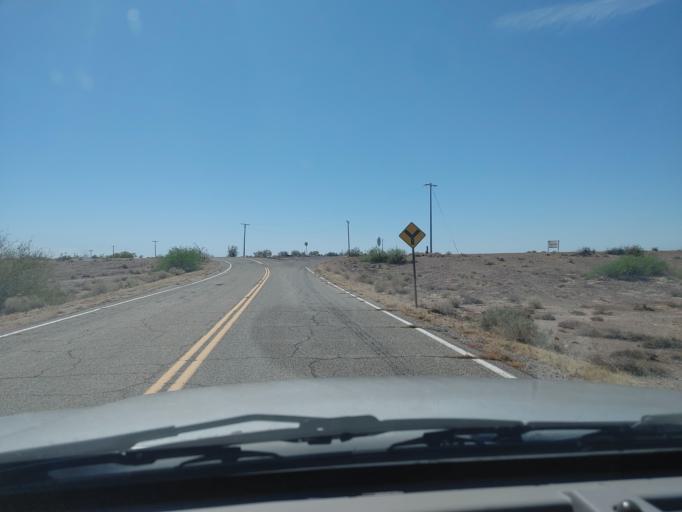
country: US
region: Arizona
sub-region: Maricopa County
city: Gila Bend
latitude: 32.9953
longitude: -113.3406
